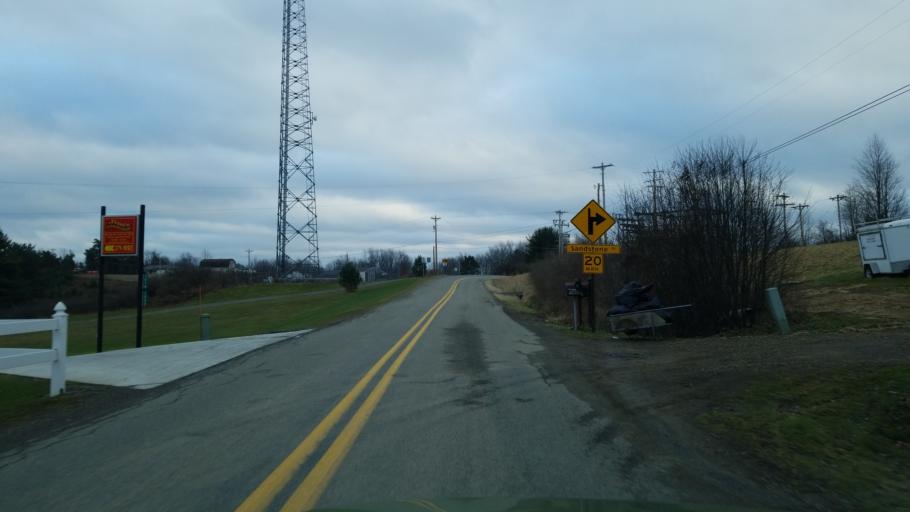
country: US
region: Pennsylvania
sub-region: Jefferson County
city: Falls Creek
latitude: 41.1671
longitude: -78.8108
